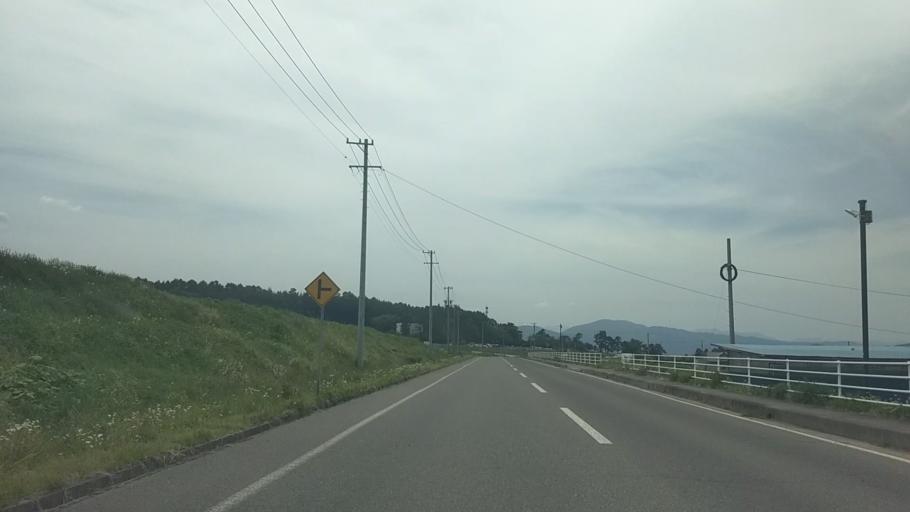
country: JP
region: Nagano
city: Chino
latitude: 36.0270
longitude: 138.2349
